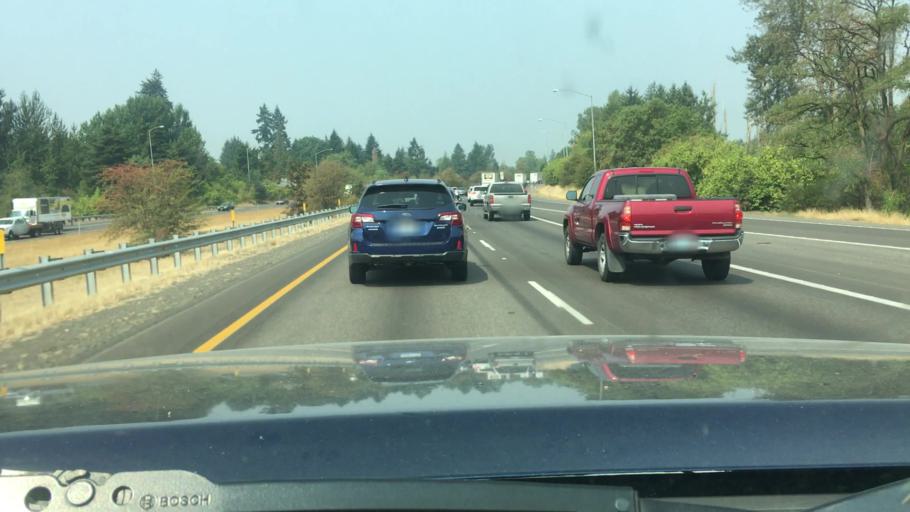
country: US
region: Oregon
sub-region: Clackamas County
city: West Linn
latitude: 45.3485
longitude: -122.6551
